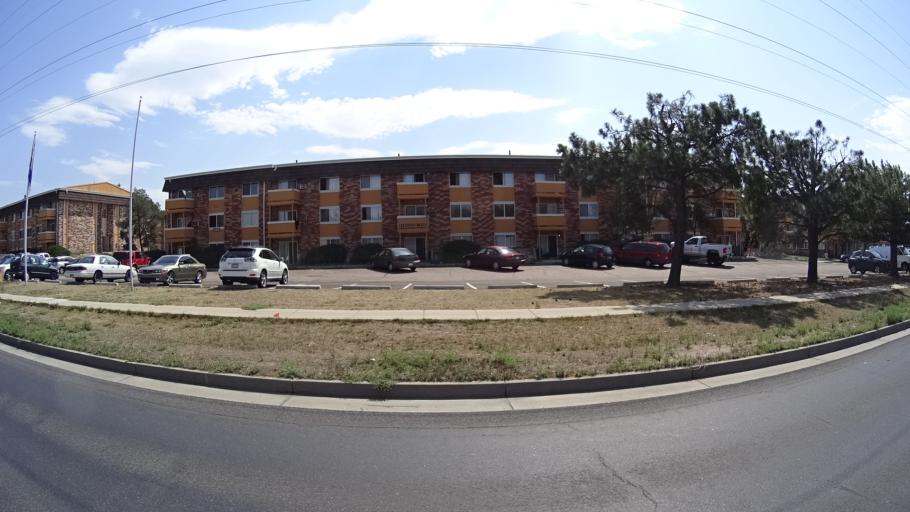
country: US
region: Colorado
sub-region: El Paso County
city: Stratmoor
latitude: 38.8295
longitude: -104.7573
